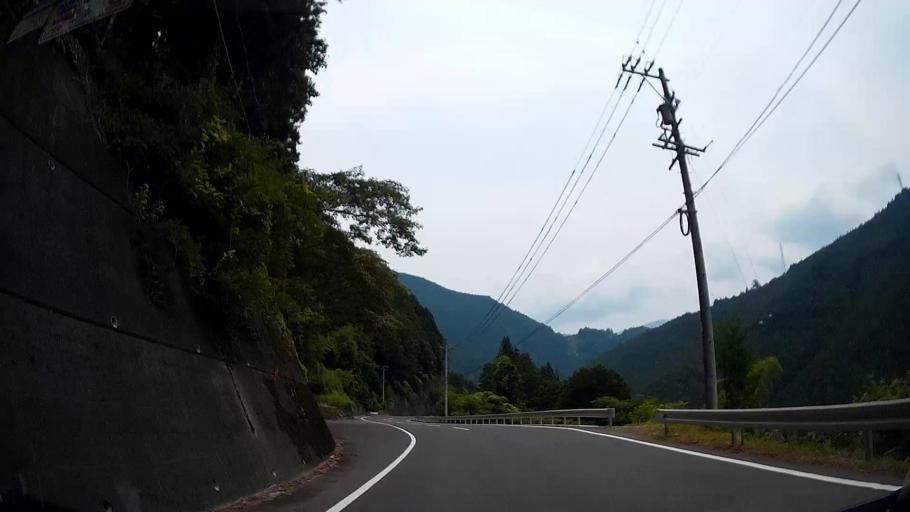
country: JP
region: Shizuoka
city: Mori
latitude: 35.0822
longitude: 137.8280
